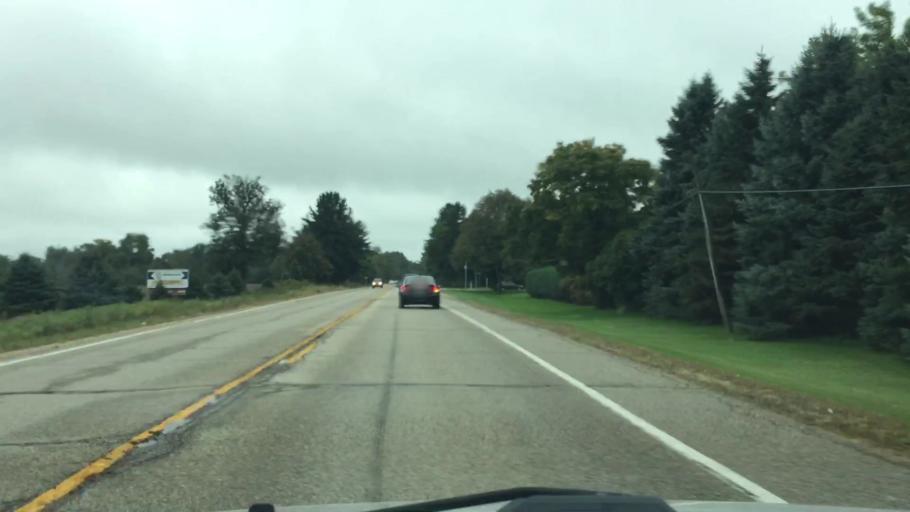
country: US
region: Wisconsin
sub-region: Rock County
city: Janesville
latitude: 42.7226
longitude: -89.0320
